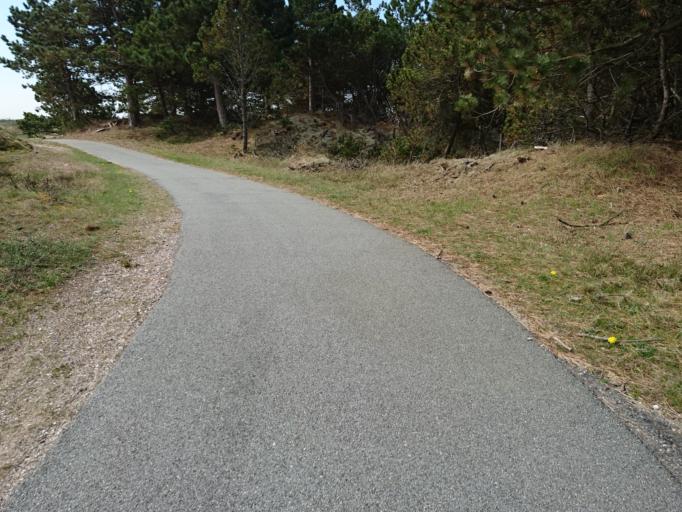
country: DK
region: North Denmark
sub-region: Frederikshavn Kommune
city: Skagen
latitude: 57.6945
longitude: 10.5040
